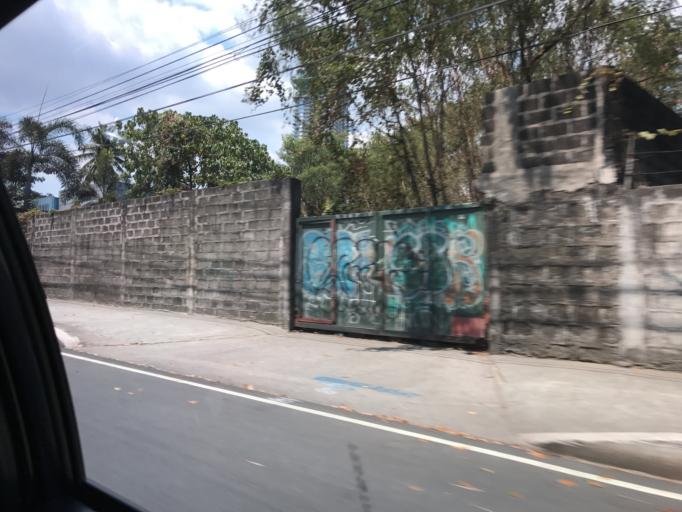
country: PH
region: Metro Manila
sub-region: Pasig
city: Pasig City
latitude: 14.5973
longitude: 121.0530
